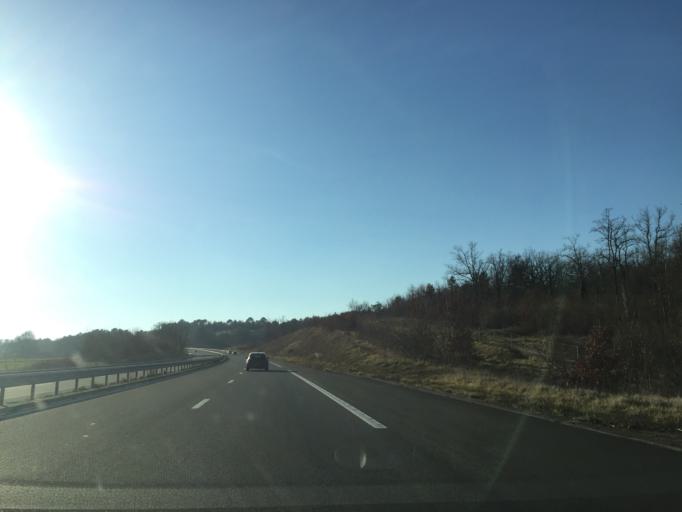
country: FR
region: Aquitaine
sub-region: Departement de la Dordogne
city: Thenon
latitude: 45.1752
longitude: 0.9620
